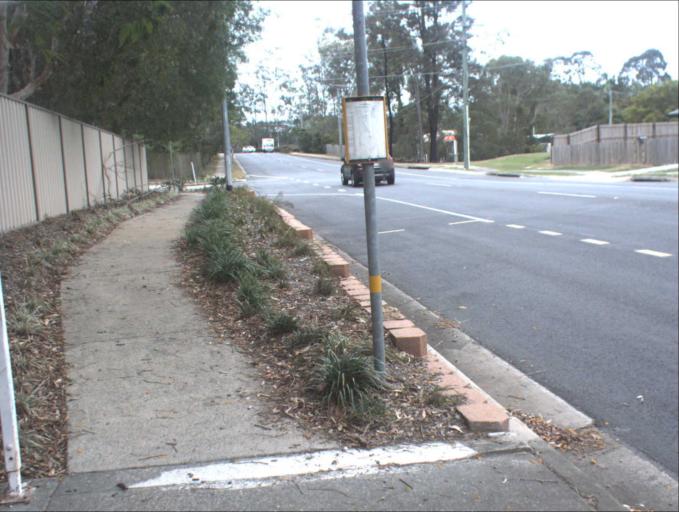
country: AU
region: Queensland
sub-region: Logan
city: Slacks Creek
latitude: -27.6755
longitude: 153.1813
